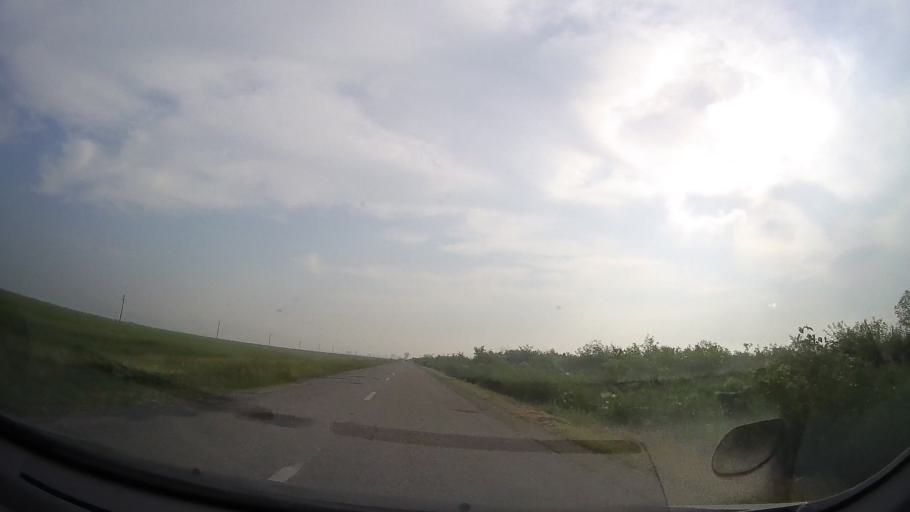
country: RO
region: Timis
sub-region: Comuna Giulvaz
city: Giulvaz
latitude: 45.5746
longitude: 21.0146
